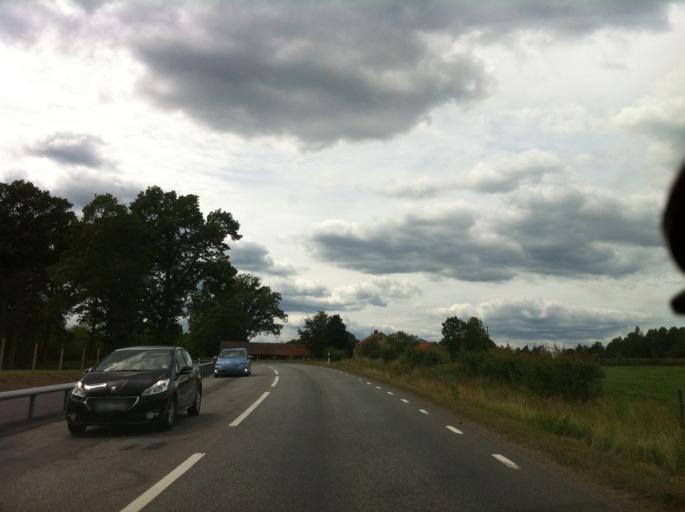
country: SE
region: Kronoberg
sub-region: Tingsryds Kommun
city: Tingsryd
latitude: 56.5330
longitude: 14.8410
